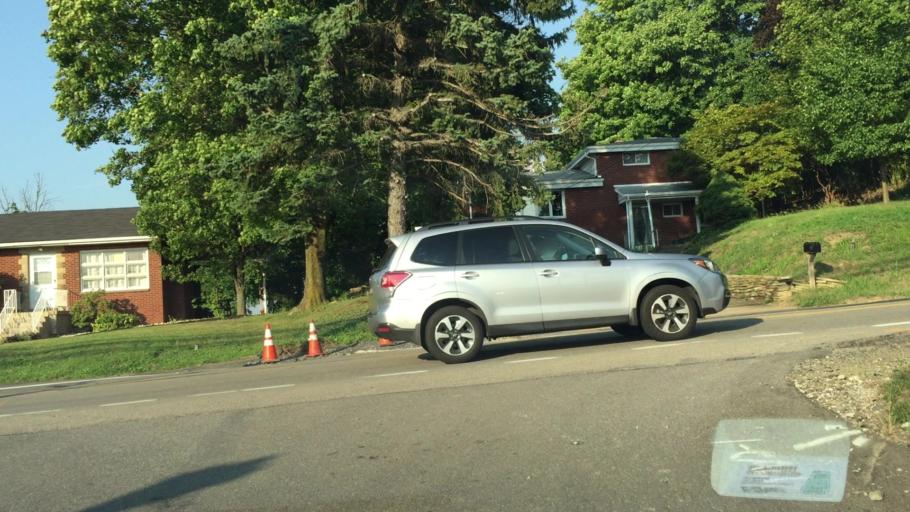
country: US
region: Pennsylvania
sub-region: Allegheny County
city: Rennerdale
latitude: 40.4541
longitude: -80.1357
